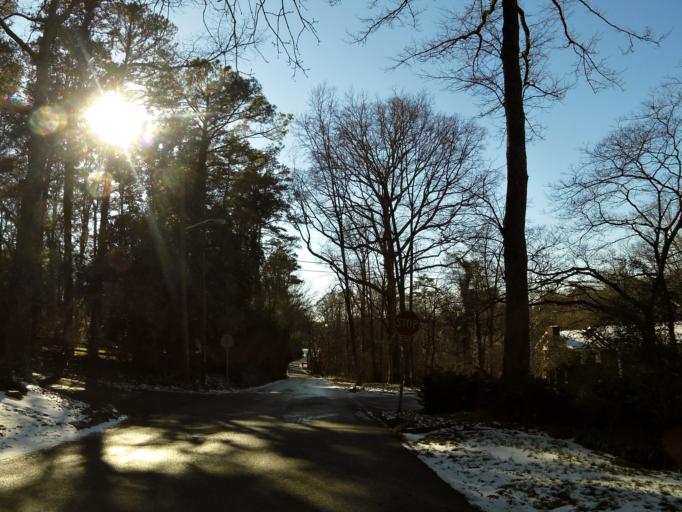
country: US
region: Tennessee
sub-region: Blount County
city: Louisville
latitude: 35.9140
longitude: -84.0144
